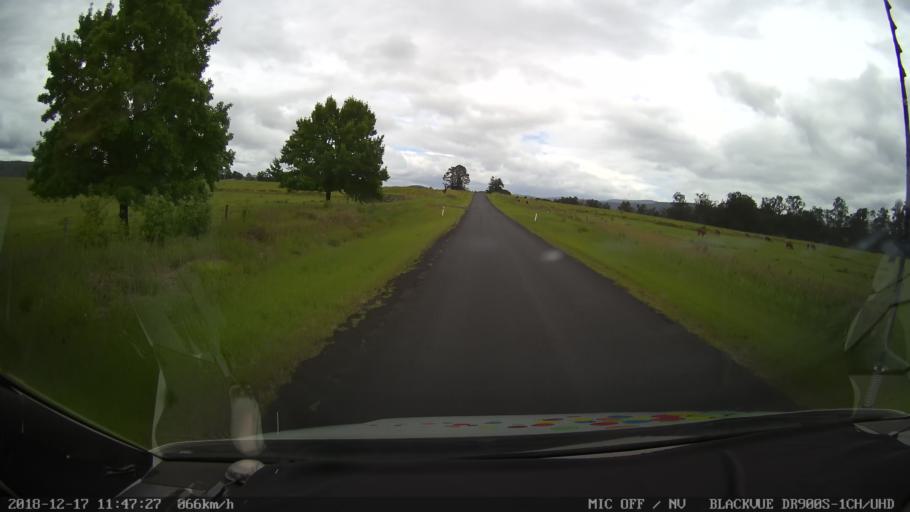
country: AU
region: New South Wales
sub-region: Kyogle
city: Kyogle
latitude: -28.6272
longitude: 152.5915
